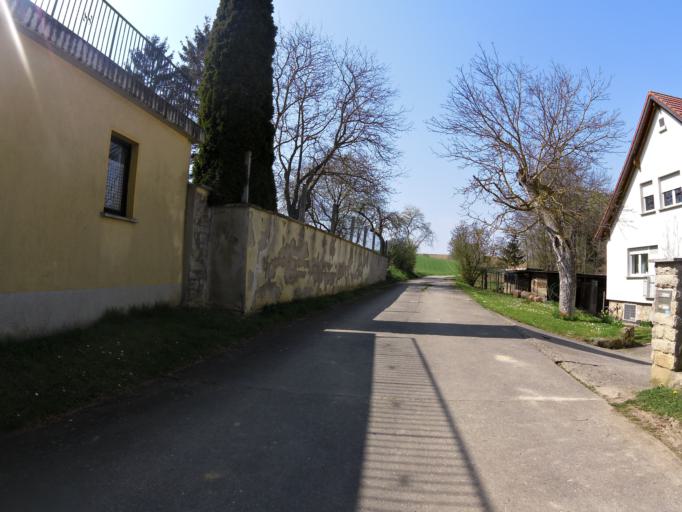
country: DE
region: Bavaria
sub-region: Regierungsbezirk Unterfranken
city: Dettelbach
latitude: 49.8181
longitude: 10.1503
